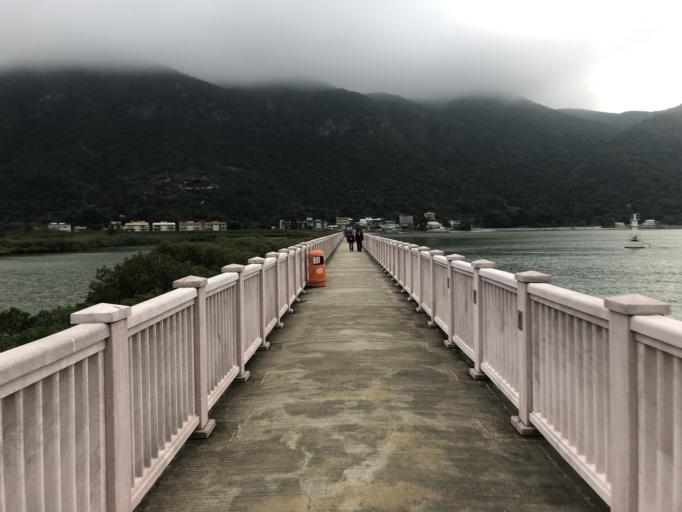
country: HK
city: Tai O
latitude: 22.2510
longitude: 113.8606
